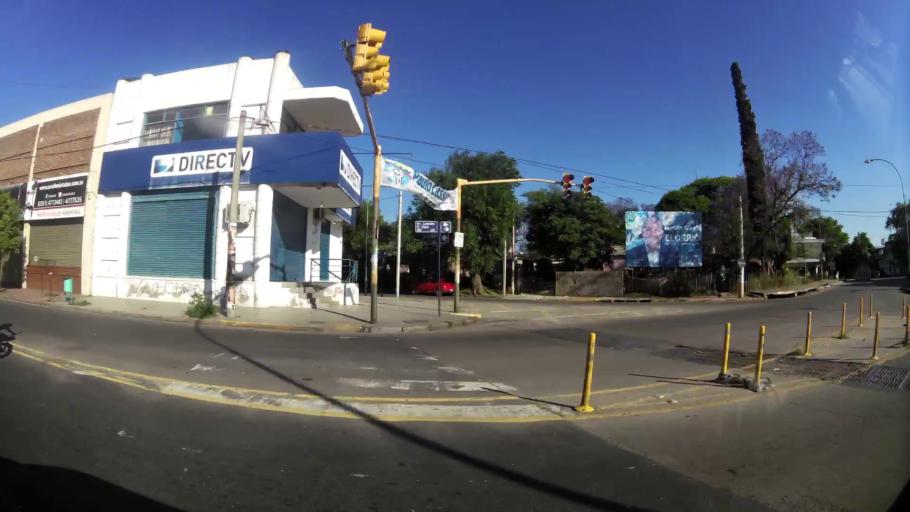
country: AR
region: Cordoba
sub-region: Departamento de Capital
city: Cordoba
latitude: -31.3988
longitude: -64.1711
